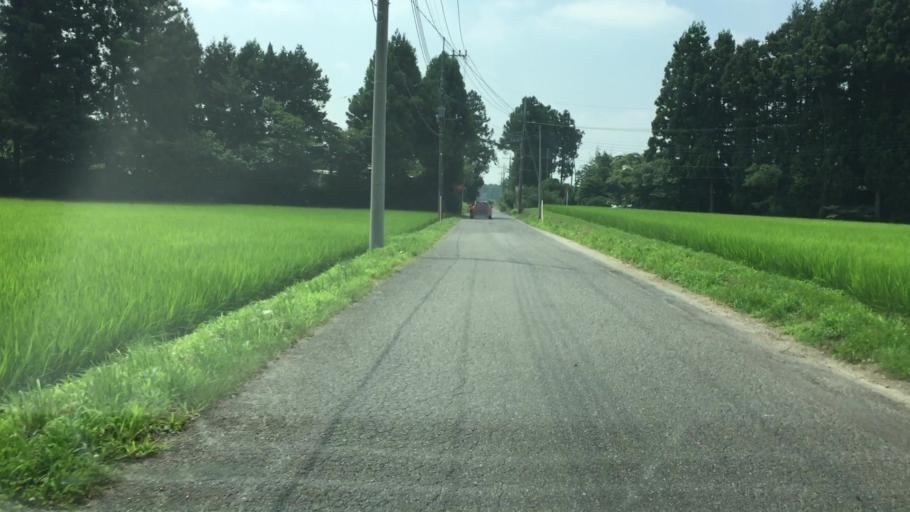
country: JP
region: Tochigi
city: Kuroiso
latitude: 36.9725
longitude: 139.9553
